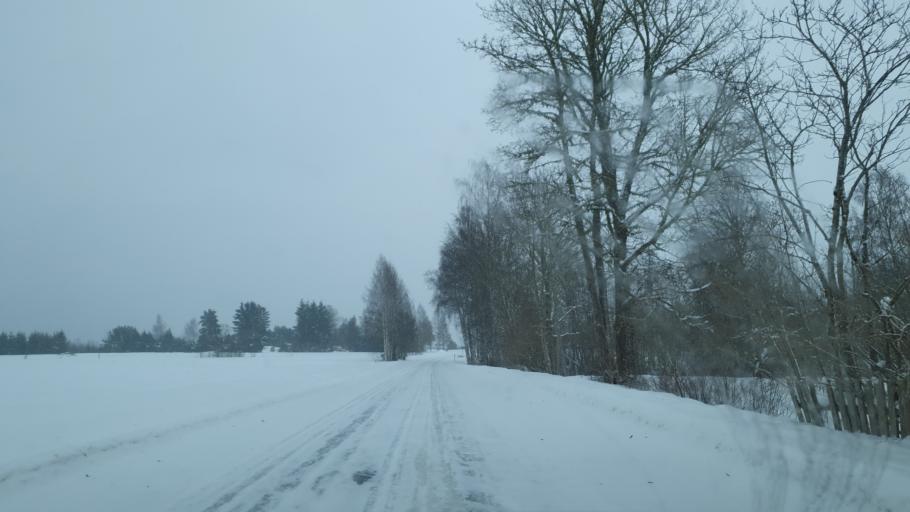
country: EE
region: Jogevamaa
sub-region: Tabivere vald
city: Tabivere
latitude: 58.5745
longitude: 26.7706
